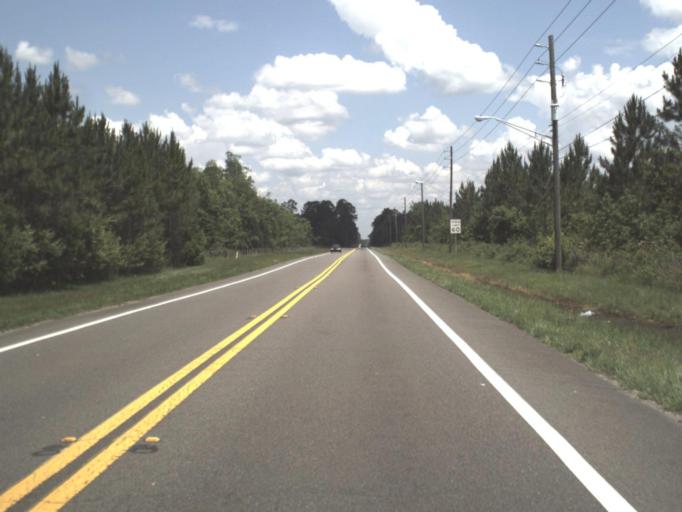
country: US
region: Florida
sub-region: Nassau County
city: Nassau Village-Ratliff
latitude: 30.4942
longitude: -81.7397
